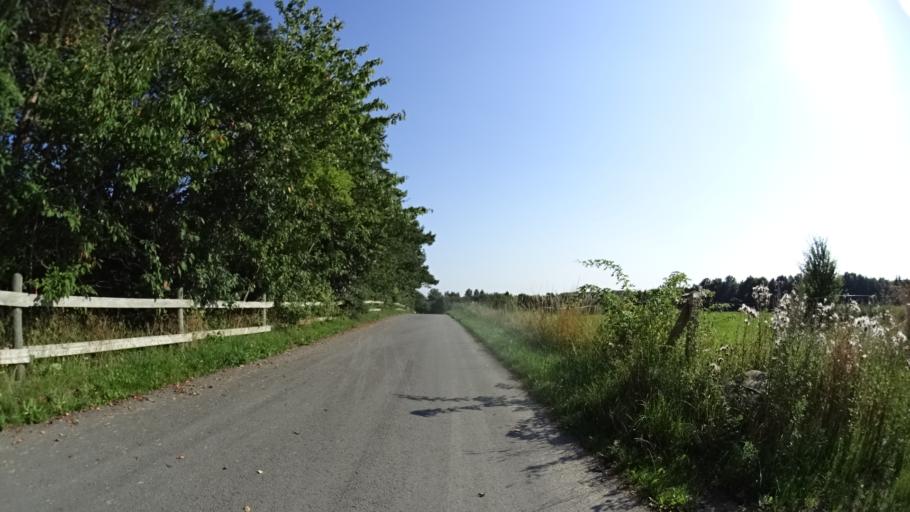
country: DK
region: Central Jutland
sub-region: Arhus Kommune
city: Stavtrup
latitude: 56.1634
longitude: 10.1176
